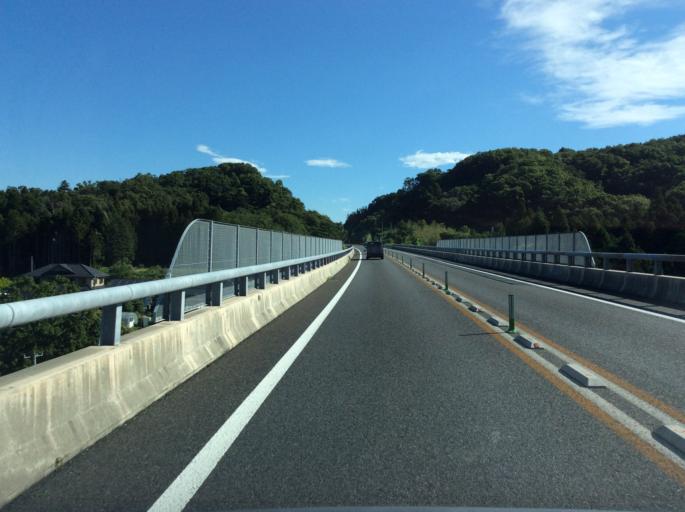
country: JP
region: Fukushima
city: Iwaki
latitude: 37.1458
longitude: 140.9645
